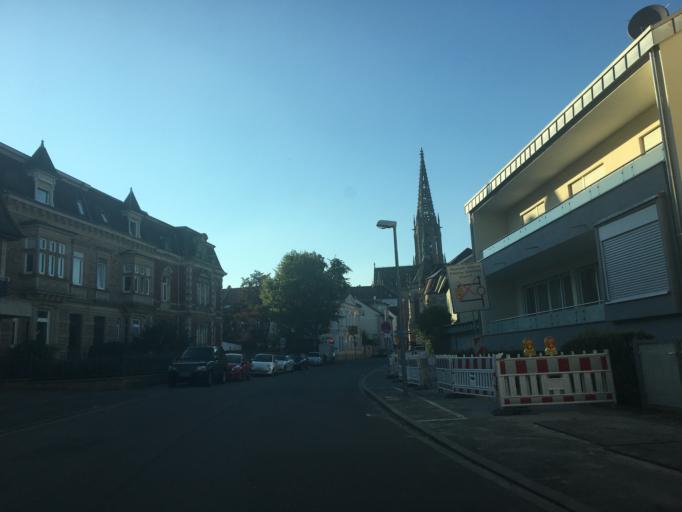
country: DE
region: Rheinland-Pfalz
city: Speyer
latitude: 49.3135
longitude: 8.4325
